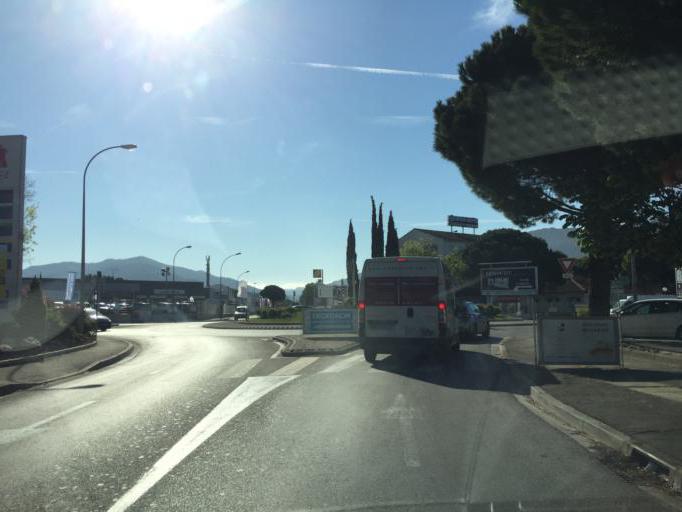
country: FR
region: Provence-Alpes-Cote d'Azur
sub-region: Departement des Bouches-du-Rhone
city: Aubagne
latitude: 43.2916
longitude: 5.5929
